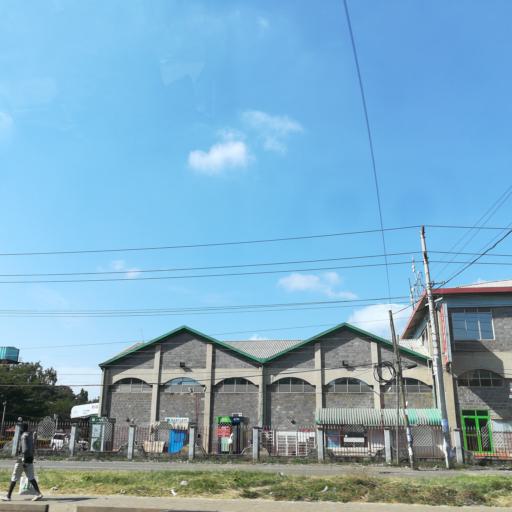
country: KE
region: Nairobi Area
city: Nairobi
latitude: -1.2996
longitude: 36.7908
